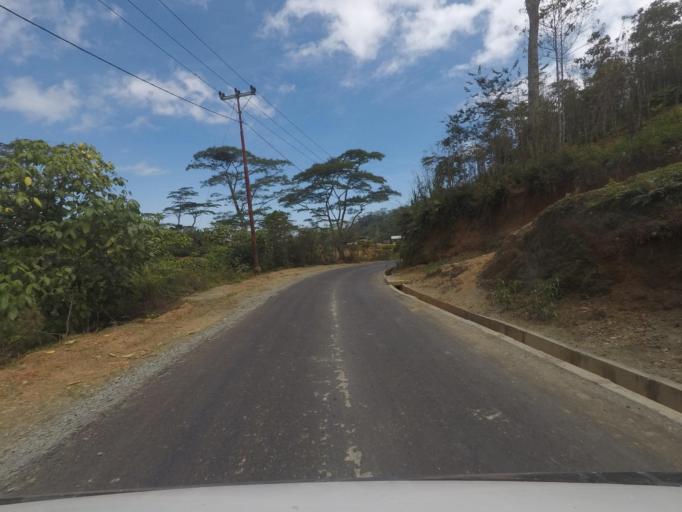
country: TL
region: Ermera
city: Gleno
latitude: -8.7467
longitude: 125.3482
